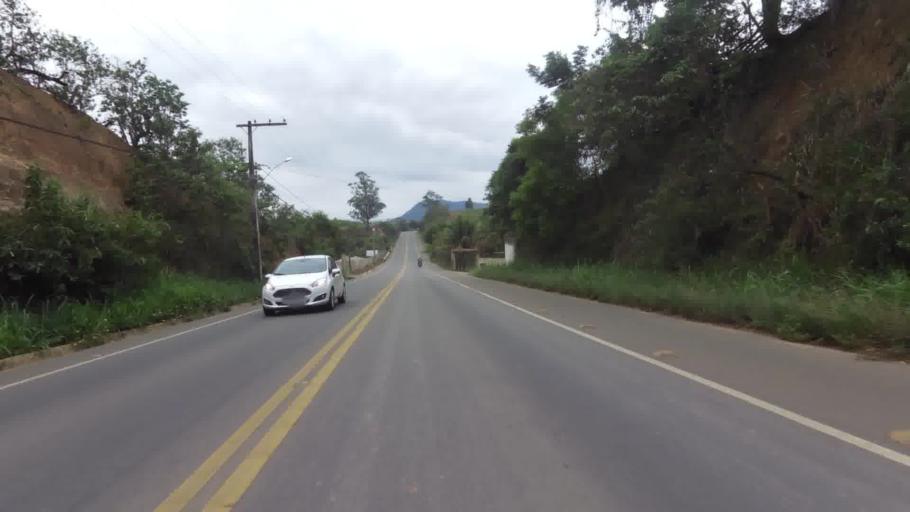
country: BR
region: Espirito Santo
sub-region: Piuma
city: Piuma
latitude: -20.8174
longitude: -40.7336
